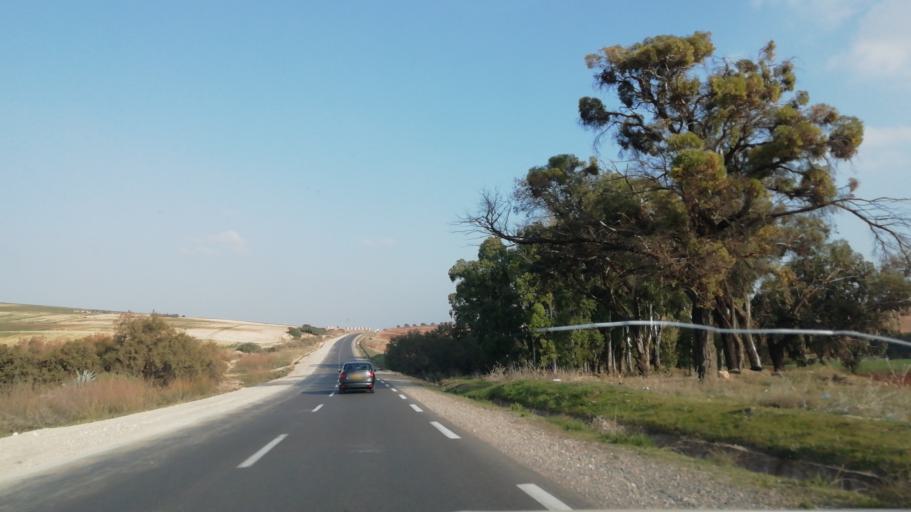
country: DZ
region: Ain Temouchent
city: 'Ain Temouchent
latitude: 35.3028
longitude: -1.0702
